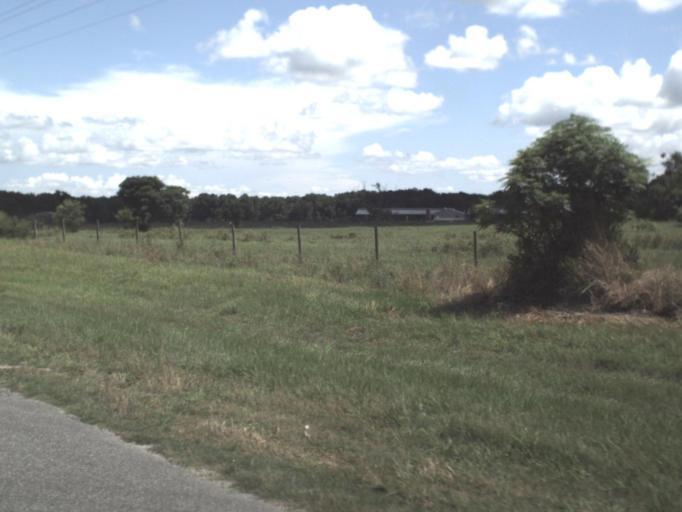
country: US
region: Florida
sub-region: Lafayette County
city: Mayo
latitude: 30.0387
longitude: -83.0705
